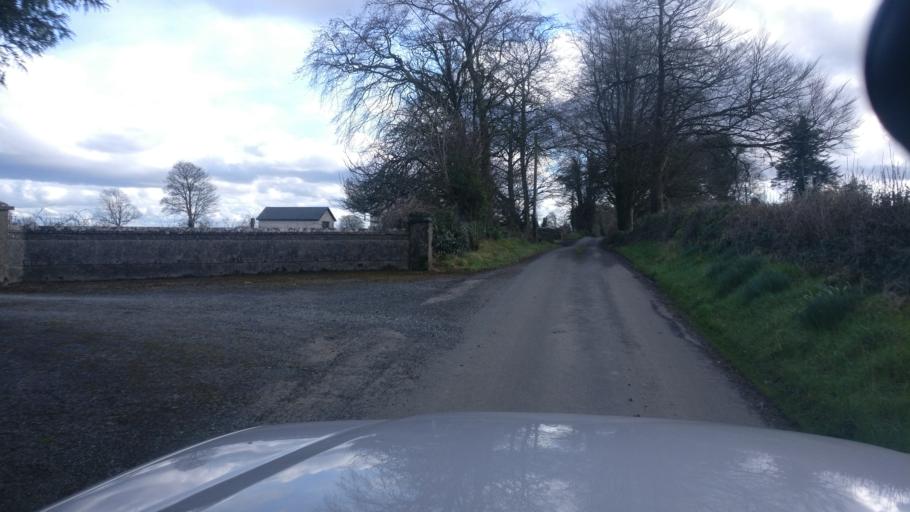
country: IE
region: Connaught
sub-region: County Galway
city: Loughrea
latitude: 53.1808
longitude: -8.4257
